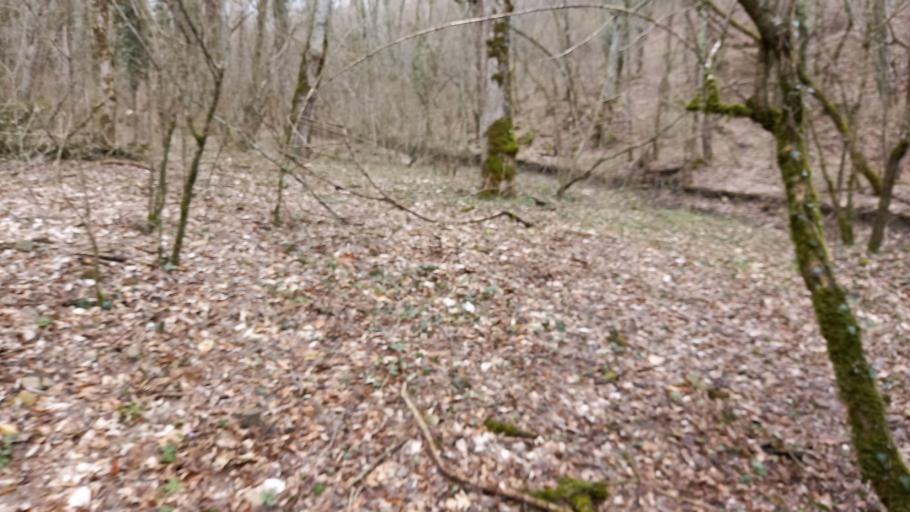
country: RU
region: Krasnodarskiy
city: Pshada
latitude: 44.4928
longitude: 38.3878
